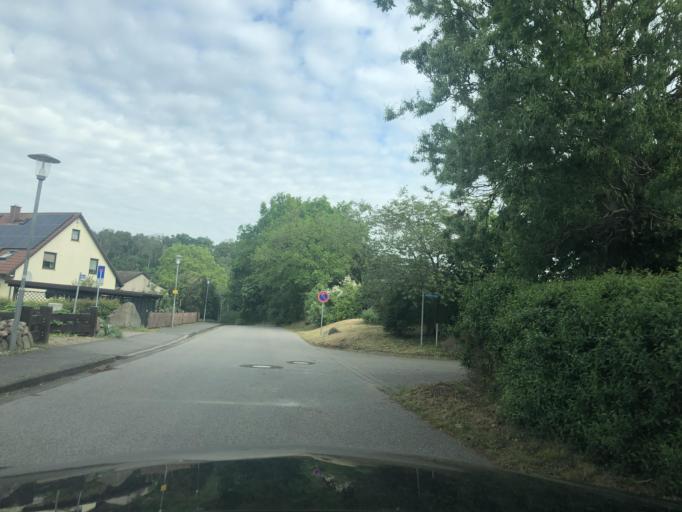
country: DE
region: Mecklenburg-Vorpommern
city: Trollenhagen
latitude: 53.6226
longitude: 13.2756
